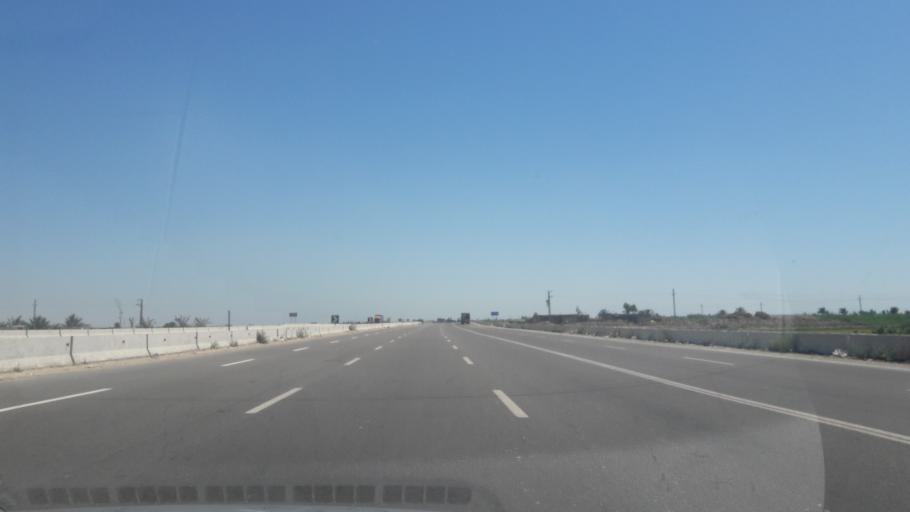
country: EG
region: Muhafazat Bur Sa`id
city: Port Said
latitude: 31.1584
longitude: 32.2352
